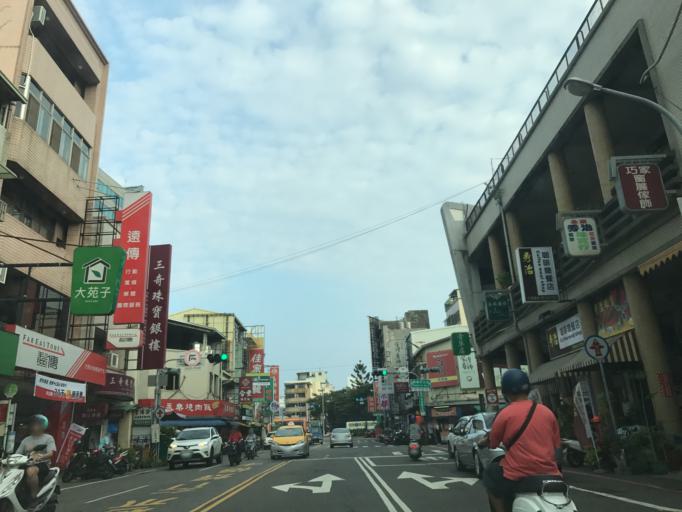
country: TW
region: Taiwan
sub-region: Tainan
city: Tainan
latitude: 22.9979
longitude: 120.1986
